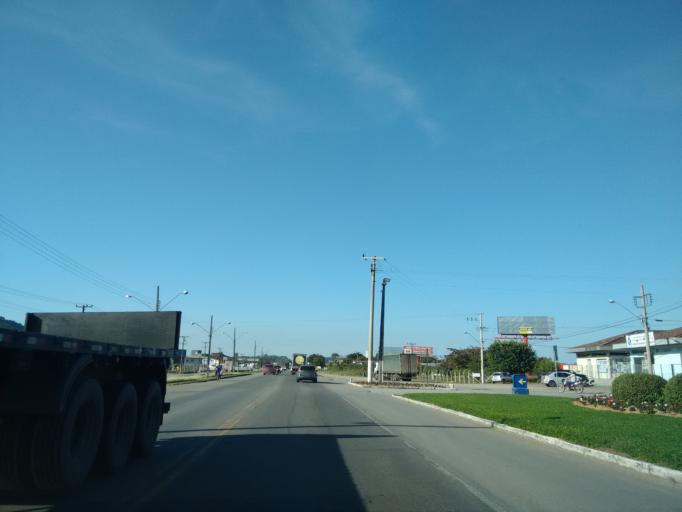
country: BR
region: Santa Catarina
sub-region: Guaramirim
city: Guaramirim
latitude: -26.4749
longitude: -48.9810
